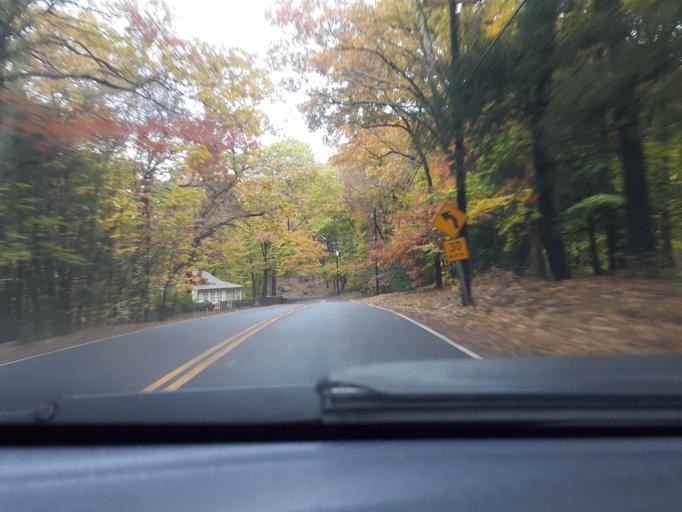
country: US
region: Connecticut
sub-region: New Haven County
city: Guilford
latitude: 41.3378
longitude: -72.7102
